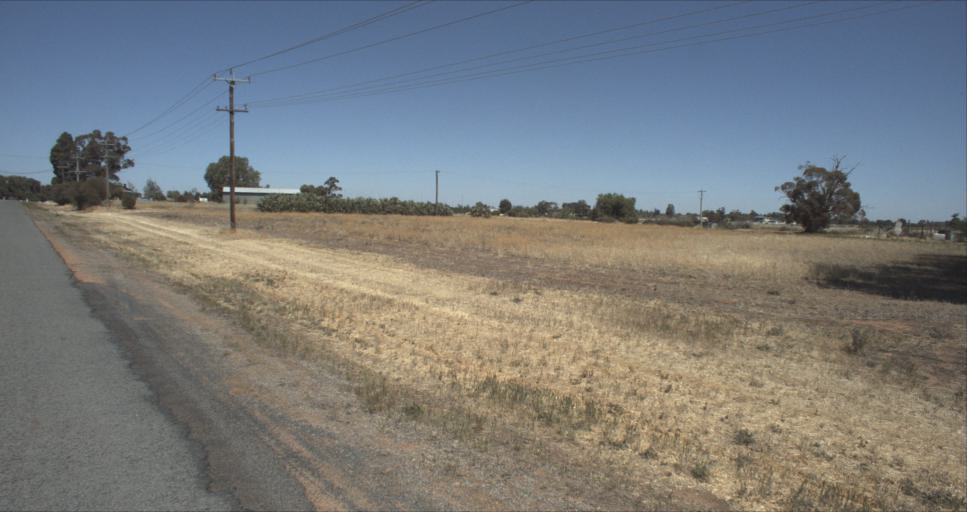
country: AU
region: New South Wales
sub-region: Leeton
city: Leeton
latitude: -34.5380
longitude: 146.3956
